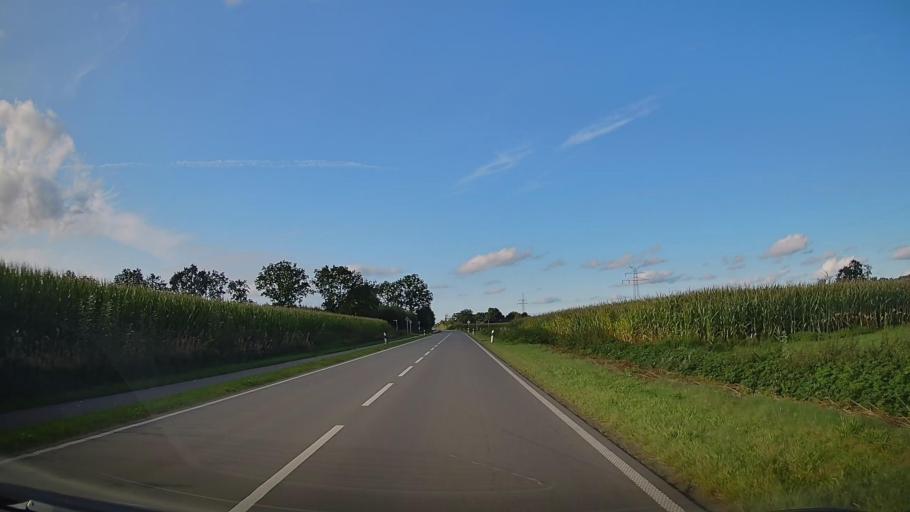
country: DE
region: Lower Saxony
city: Barssel
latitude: 53.1038
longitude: 7.7093
